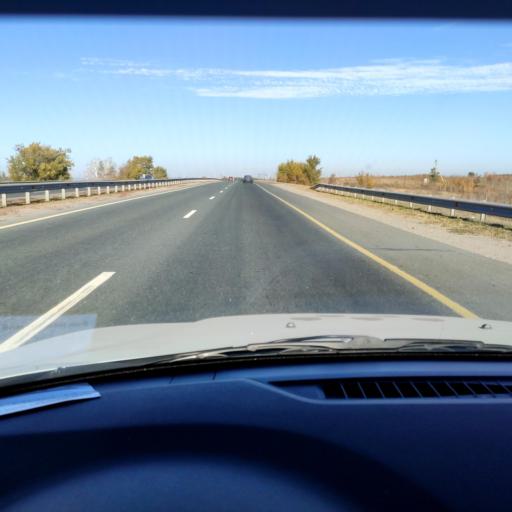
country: RU
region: Samara
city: Zhigulevsk
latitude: 53.5116
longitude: 49.5380
